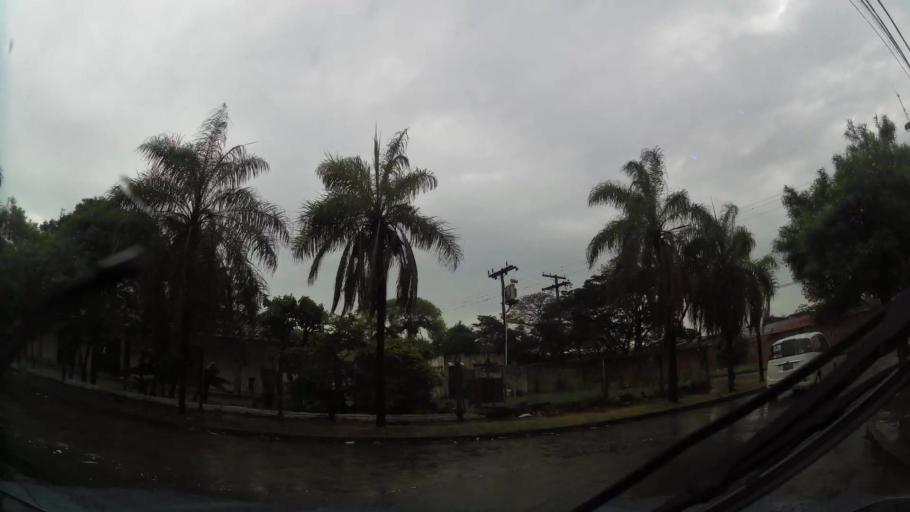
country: BO
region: Santa Cruz
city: Santa Cruz de la Sierra
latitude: -17.7975
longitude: -63.1649
